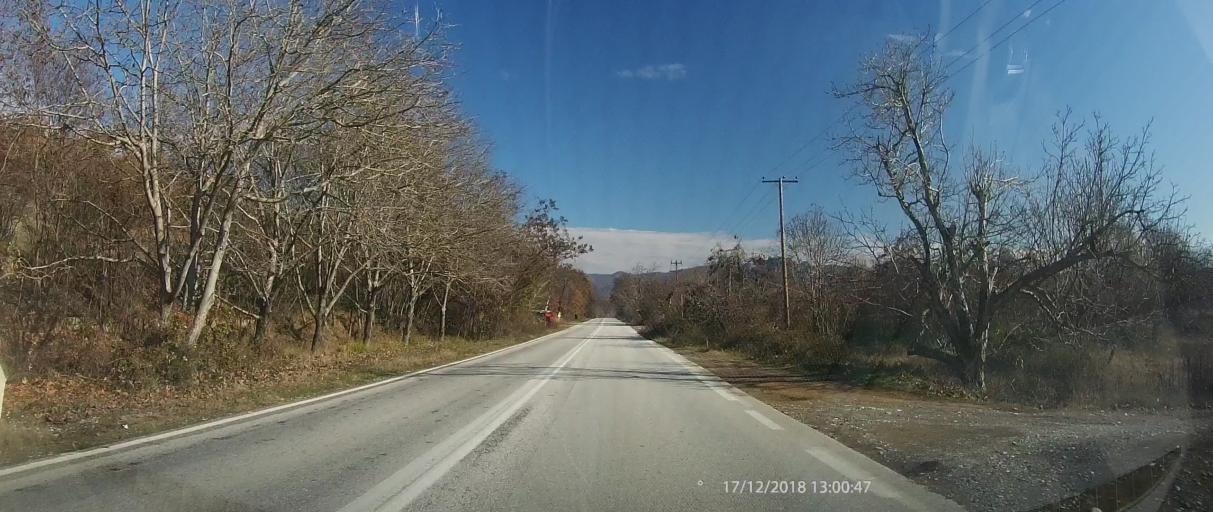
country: GR
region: Thessaly
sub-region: Trikala
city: Kastraki
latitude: 39.7315
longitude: 21.5709
